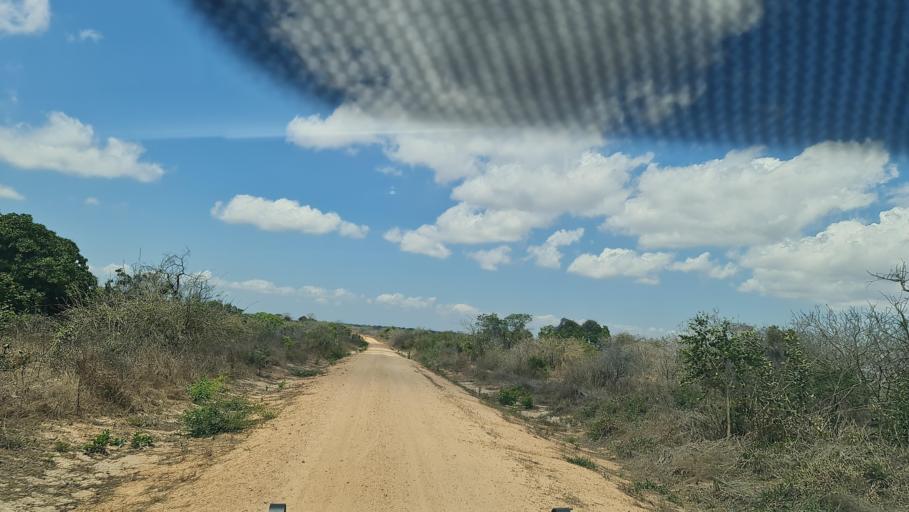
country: MZ
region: Nampula
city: Nacala
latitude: -14.3188
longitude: 40.5860
